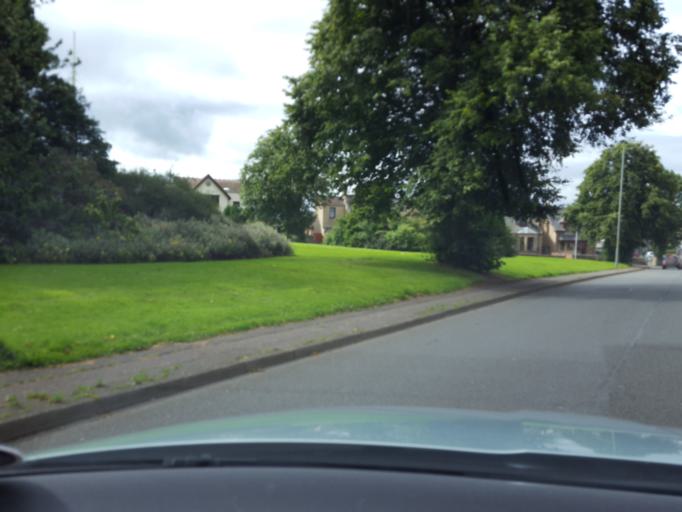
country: GB
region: Scotland
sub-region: Falkirk
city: Bo'ness
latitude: 56.0132
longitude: -3.6001
